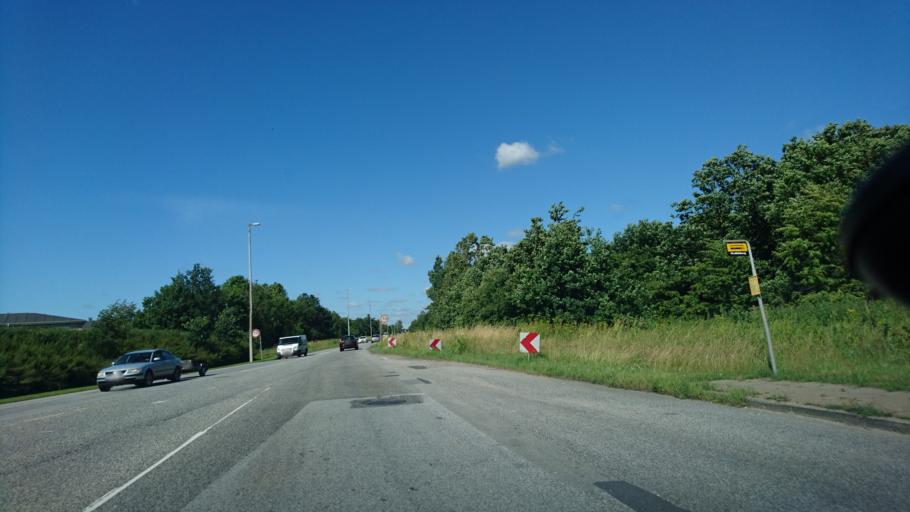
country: DK
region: North Denmark
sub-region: Alborg Kommune
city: Gistrup
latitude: 57.0249
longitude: 10.0076
